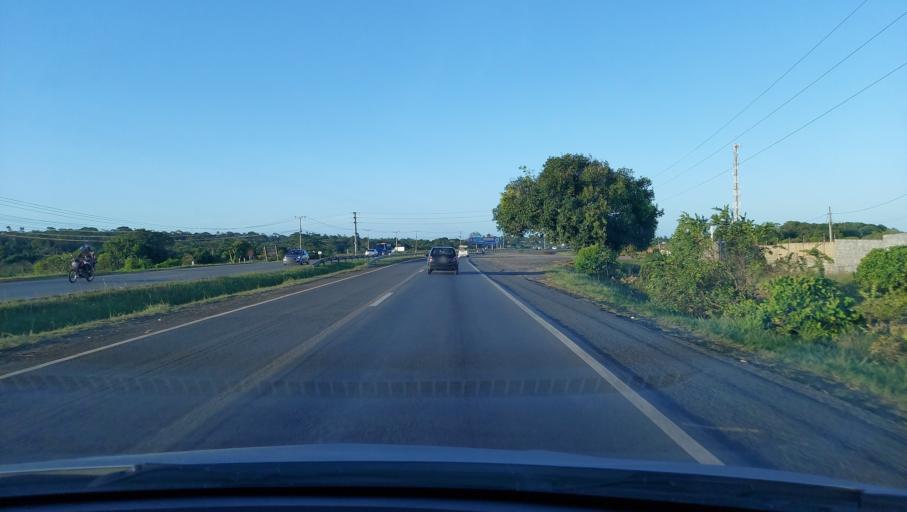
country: BR
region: Bahia
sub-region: Camacari
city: Camacari
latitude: -12.7264
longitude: -38.1608
